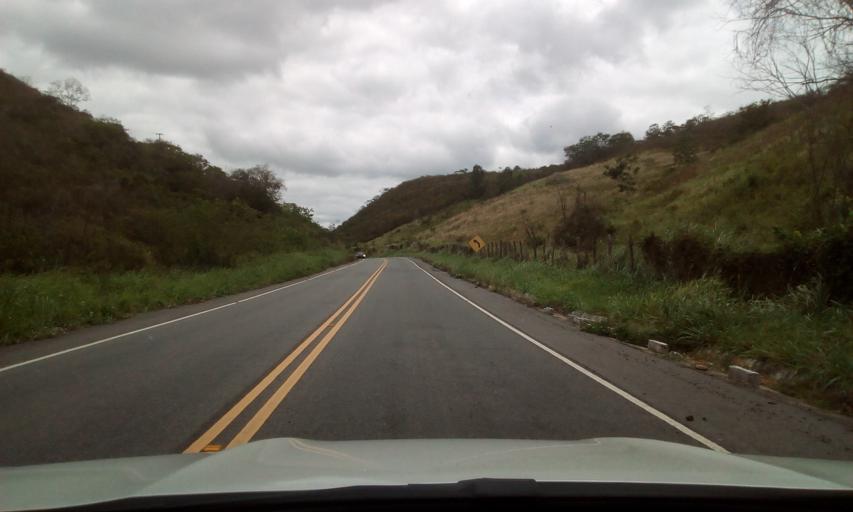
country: BR
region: Paraiba
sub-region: Serra Redonda
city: Alagoa Grande
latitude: -7.1422
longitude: -35.6143
